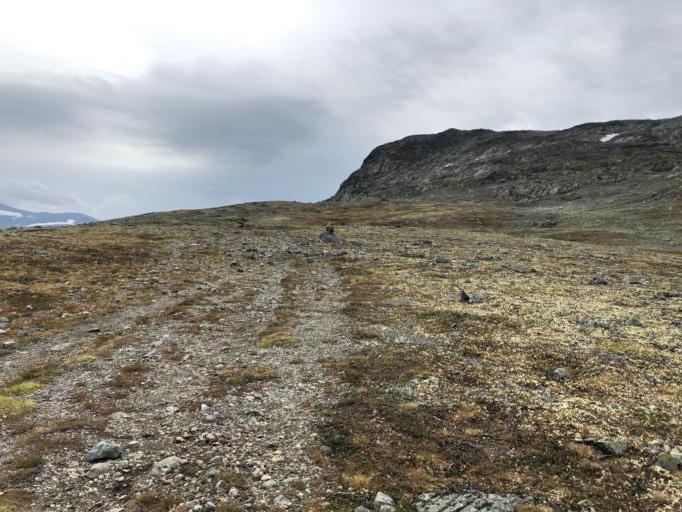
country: NO
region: Oppland
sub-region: Lom
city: Fossbergom
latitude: 61.5195
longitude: 8.8109
